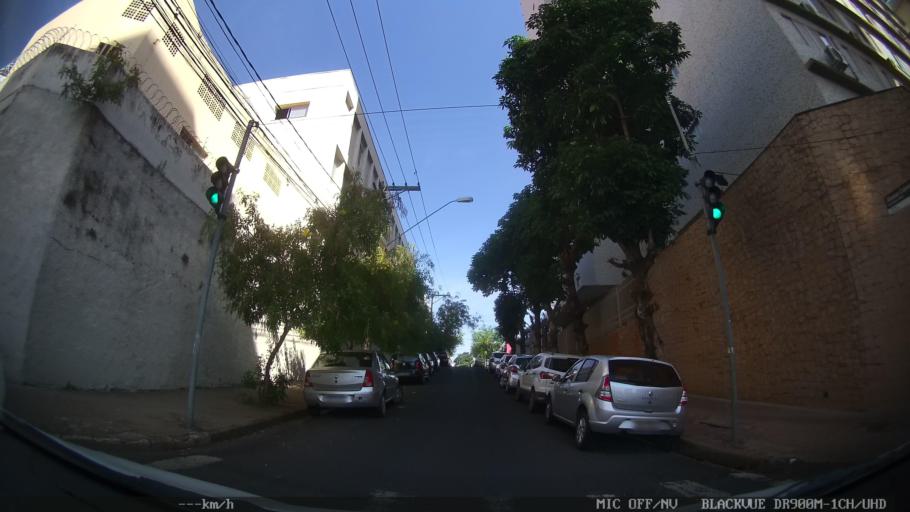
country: BR
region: Sao Paulo
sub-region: Ribeirao Preto
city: Ribeirao Preto
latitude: -21.1797
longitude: -47.8142
